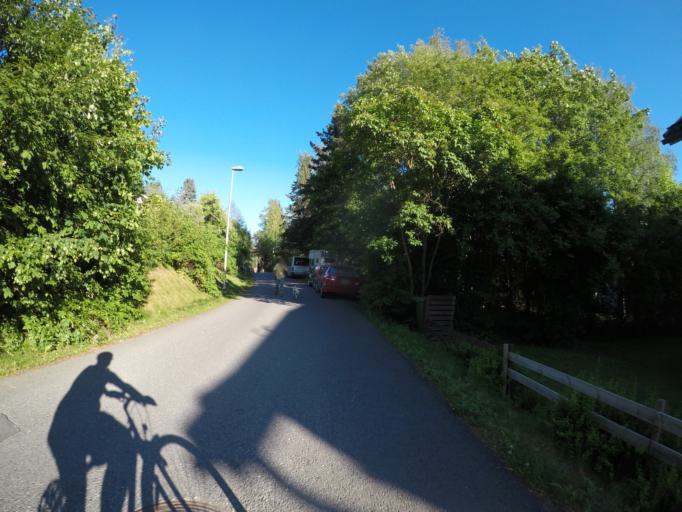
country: FI
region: Haeme
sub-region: Haemeenlinna
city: Haemeenlinna
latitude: 60.9840
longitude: 24.4469
